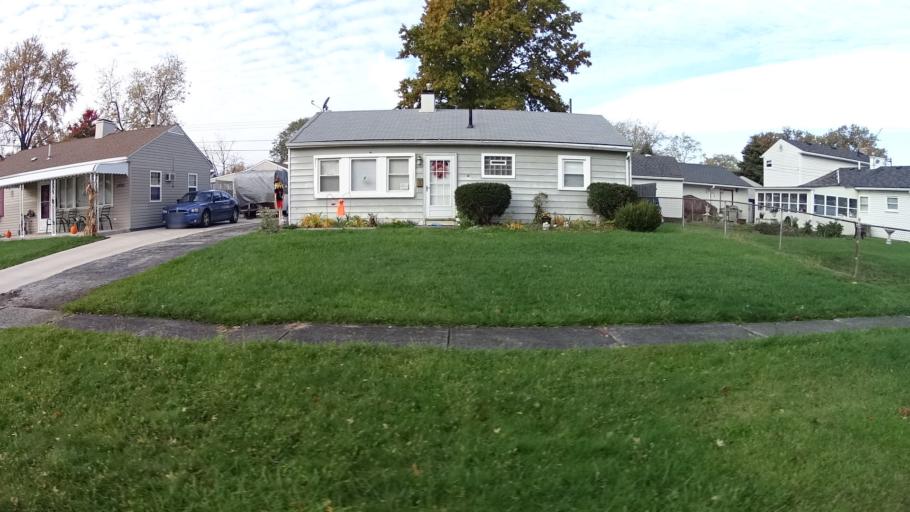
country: US
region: Ohio
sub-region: Lorain County
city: Sheffield
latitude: 41.4322
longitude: -82.1111
